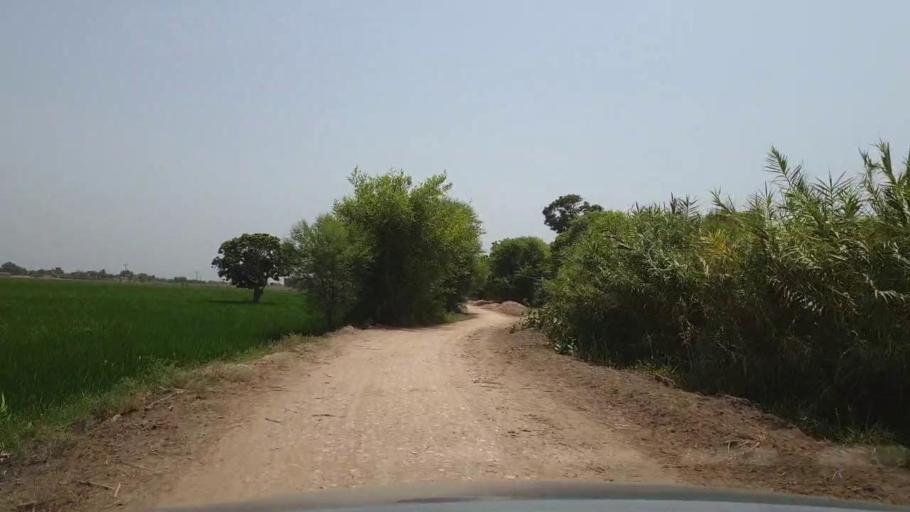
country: PK
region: Sindh
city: Ratodero
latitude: 27.7932
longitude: 68.3473
